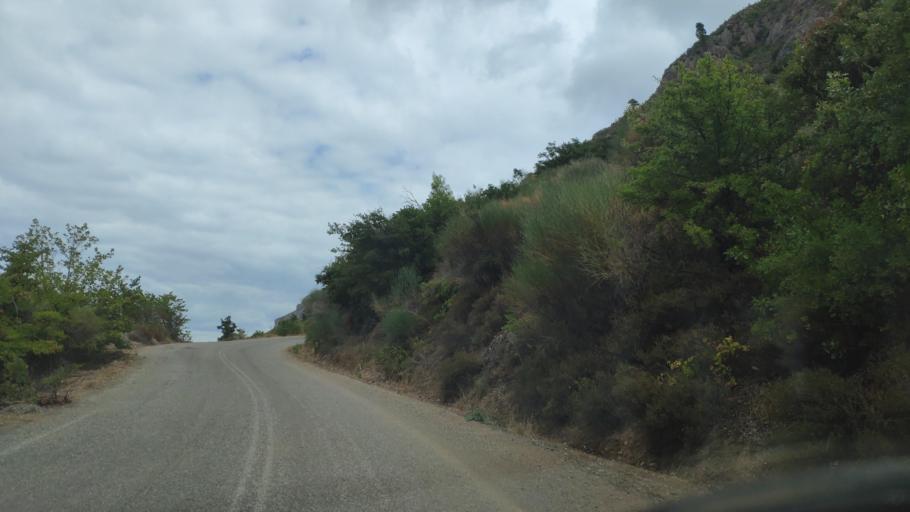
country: GR
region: West Greece
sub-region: Nomos Achaias
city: Temeni
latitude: 38.1671
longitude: 22.1407
